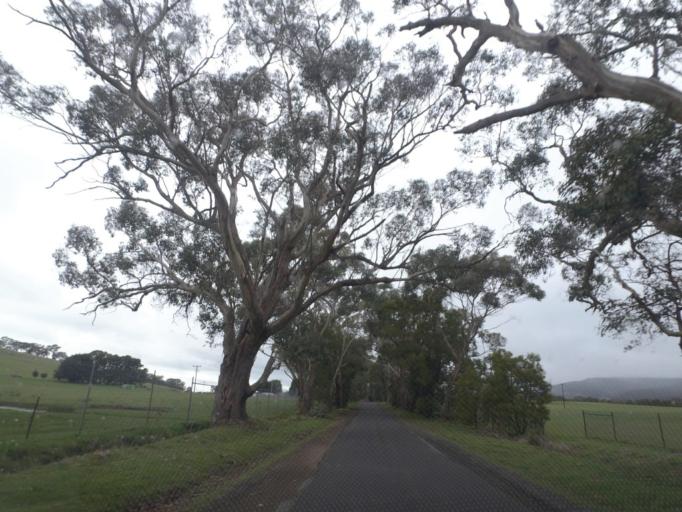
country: AU
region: Victoria
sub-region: Hume
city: Sunbury
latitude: -37.3288
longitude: 144.6025
